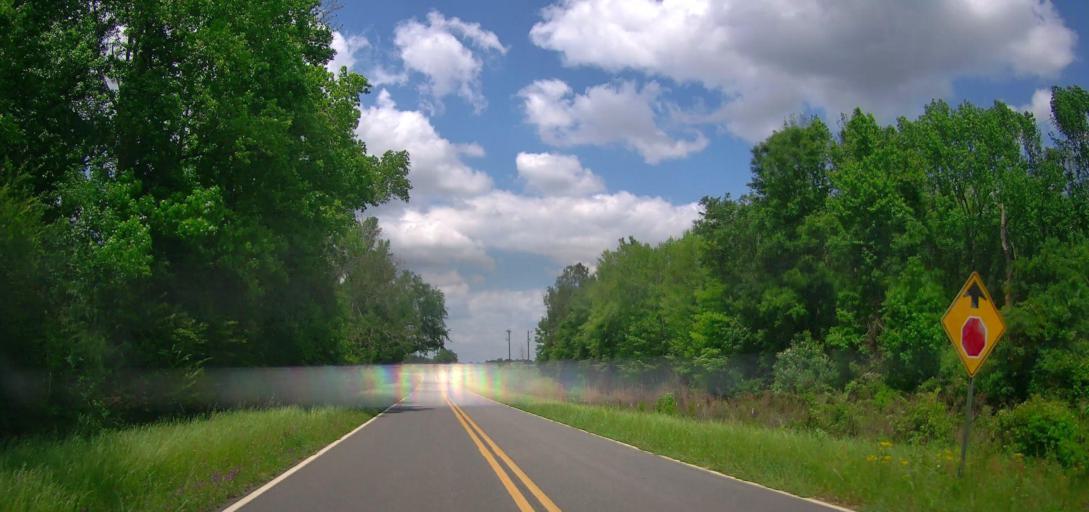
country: US
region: Georgia
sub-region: Laurens County
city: East Dublin
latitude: 32.6358
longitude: -82.8394
